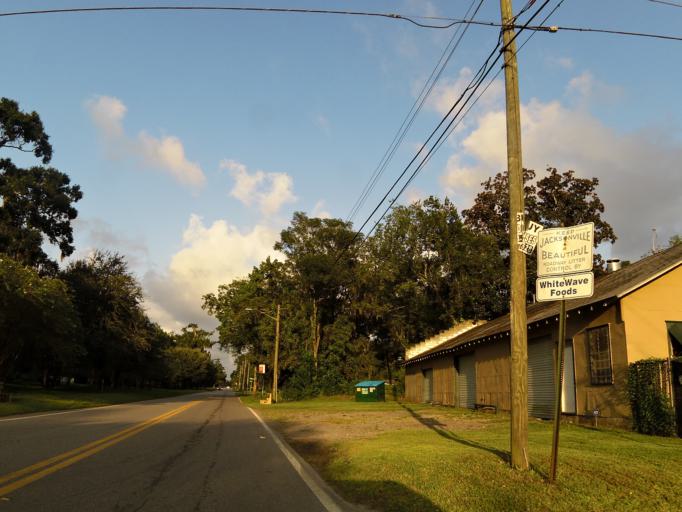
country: US
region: Florida
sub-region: Duval County
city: Jacksonville
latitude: 30.3265
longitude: -81.6968
